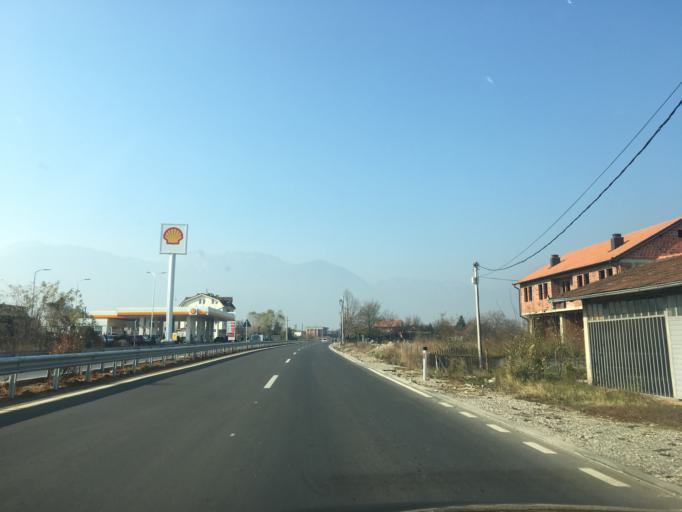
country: XK
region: Pec
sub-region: Komuna e Pejes
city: Dubova (Driloni)
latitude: 42.6587
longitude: 20.3561
